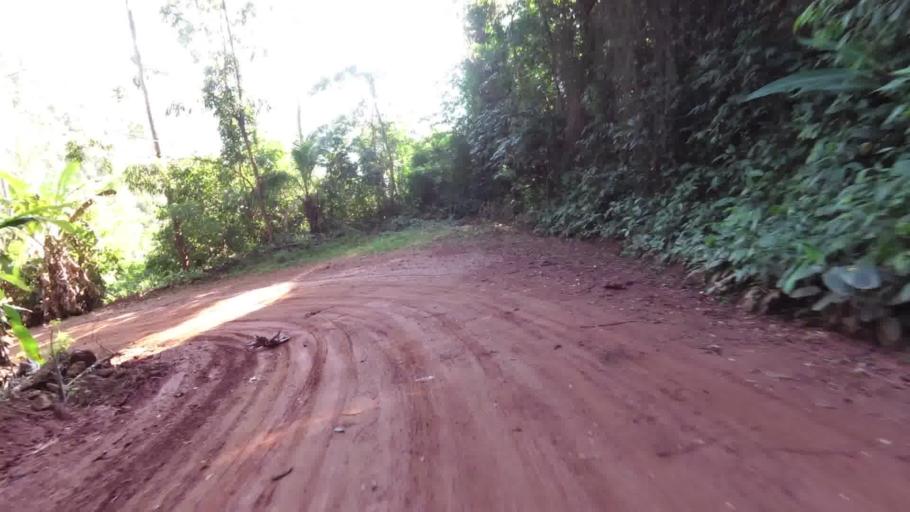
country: BR
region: Espirito Santo
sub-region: Alfredo Chaves
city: Alfredo Chaves
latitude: -20.6063
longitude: -40.7617
